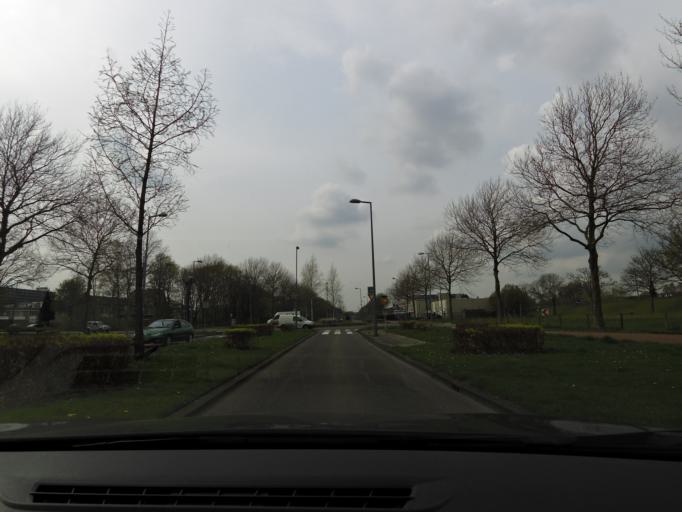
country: NL
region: South Holland
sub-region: Gemeente Spijkenisse
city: Spijkenisse
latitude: 51.8546
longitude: 4.3752
